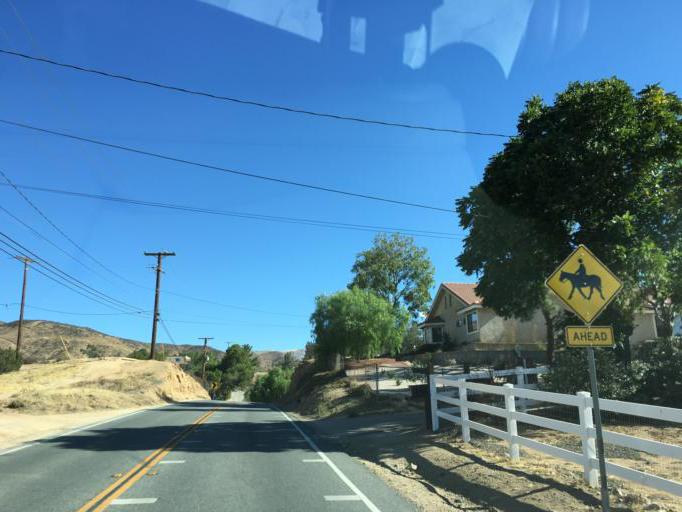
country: US
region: California
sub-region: Los Angeles County
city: Agua Dulce
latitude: 34.4989
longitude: -118.3262
